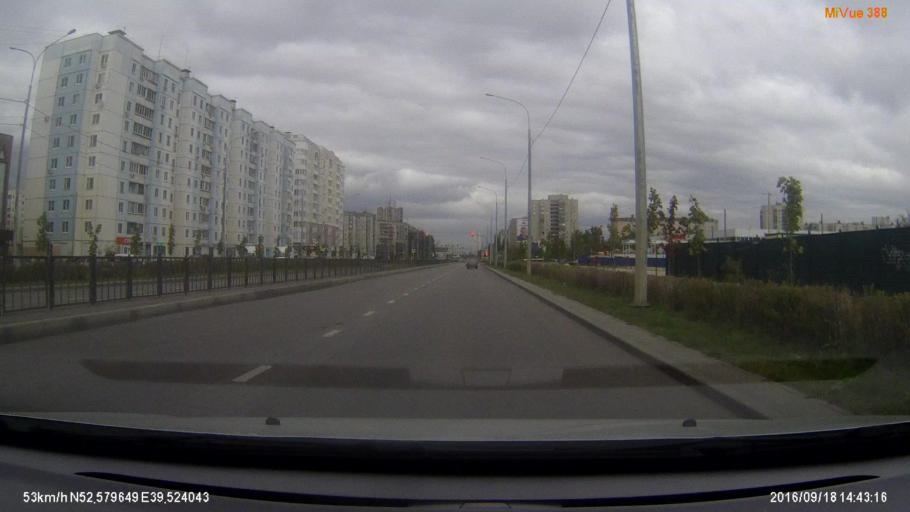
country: RU
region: Lipetsk
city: Syrskoye
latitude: 52.5797
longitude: 39.5241
